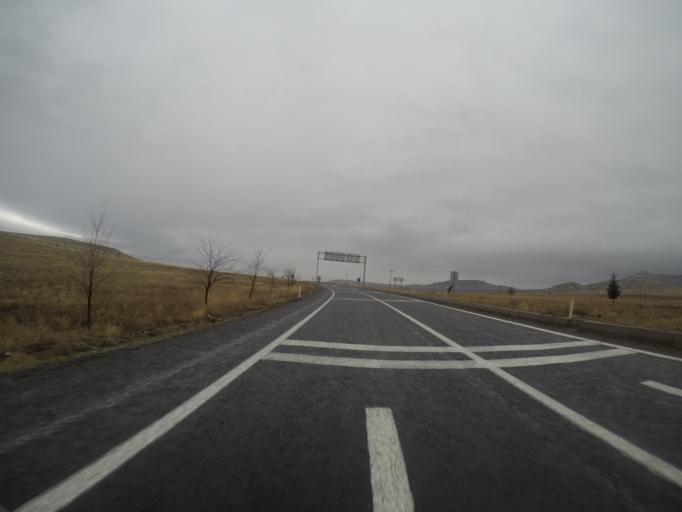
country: TR
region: Nevsehir
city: Avanos
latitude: 38.7142
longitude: 34.9320
